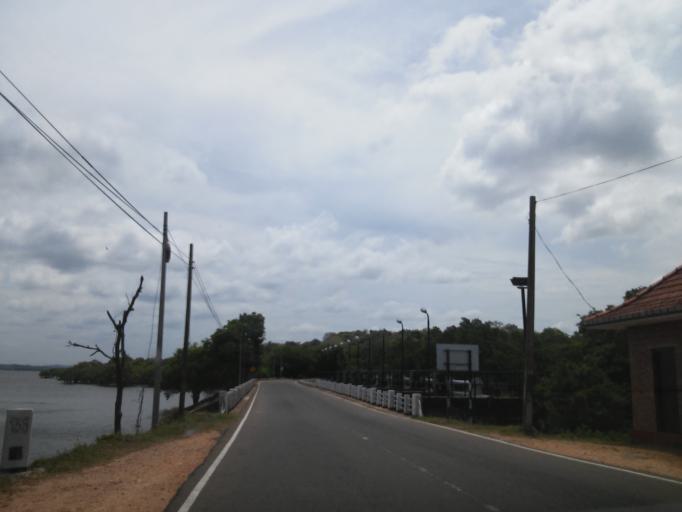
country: LK
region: Eastern Province
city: Trincomalee
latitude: 8.3407
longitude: 80.9790
